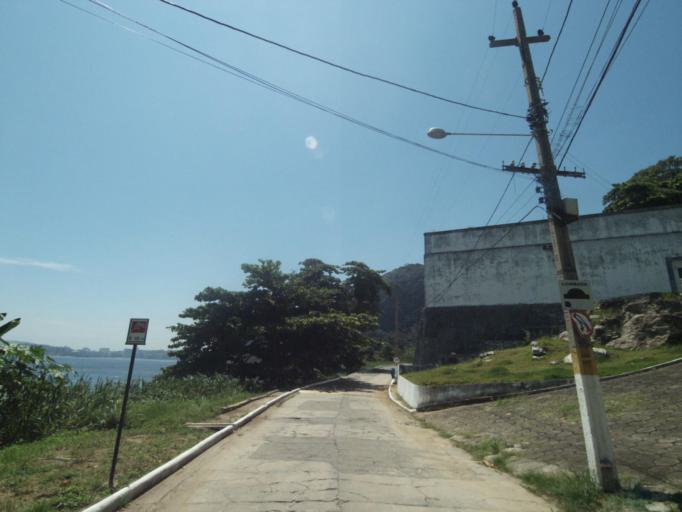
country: BR
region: Rio de Janeiro
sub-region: Niteroi
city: Niteroi
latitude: -22.9376
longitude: -43.1298
